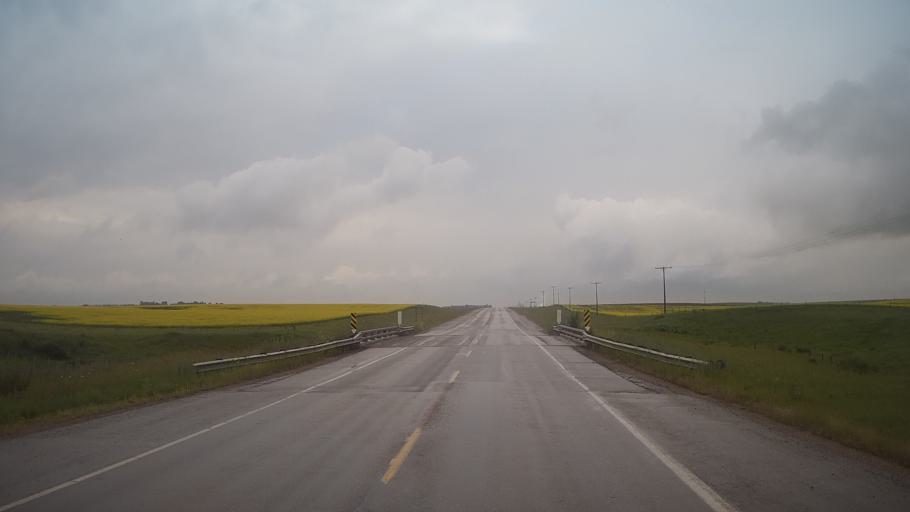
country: CA
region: Saskatchewan
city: Unity
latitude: 52.4349
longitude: -109.0427
